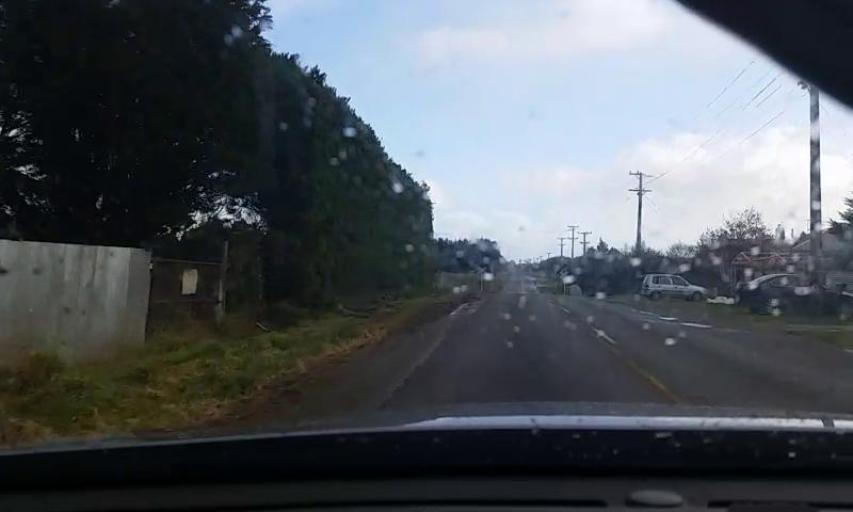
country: NZ
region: Southland
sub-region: Invercargill City
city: Invercargill
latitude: -46.3581
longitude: 168.3427
